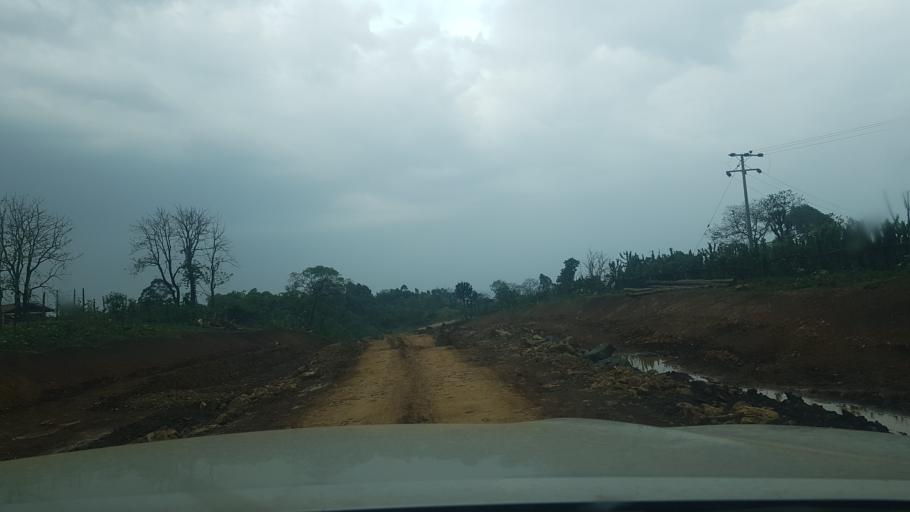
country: ET
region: Oromiya
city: Gore
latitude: 7.9172
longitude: 35.5142
